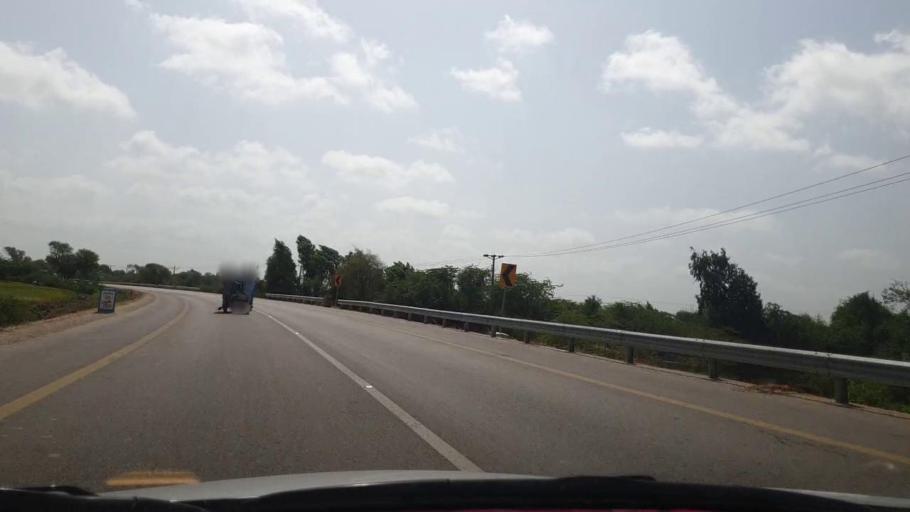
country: PK
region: Sindh
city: Talhar
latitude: 24.9102
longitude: 68.7332
